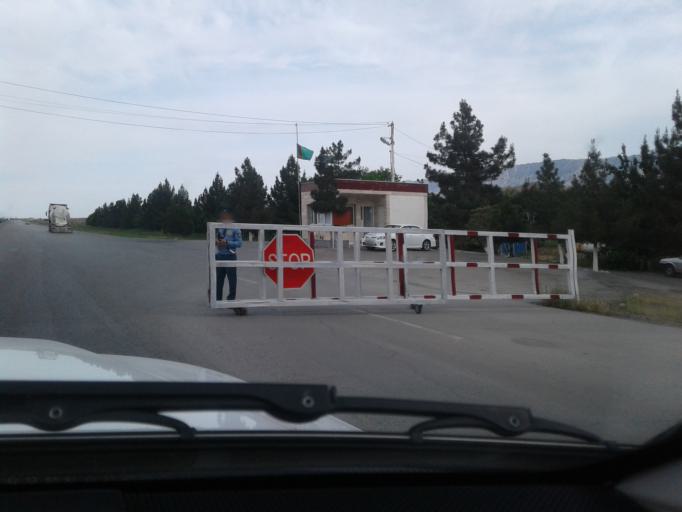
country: TM
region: Ahal
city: Baharly
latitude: 38.2441
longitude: 57.7601
